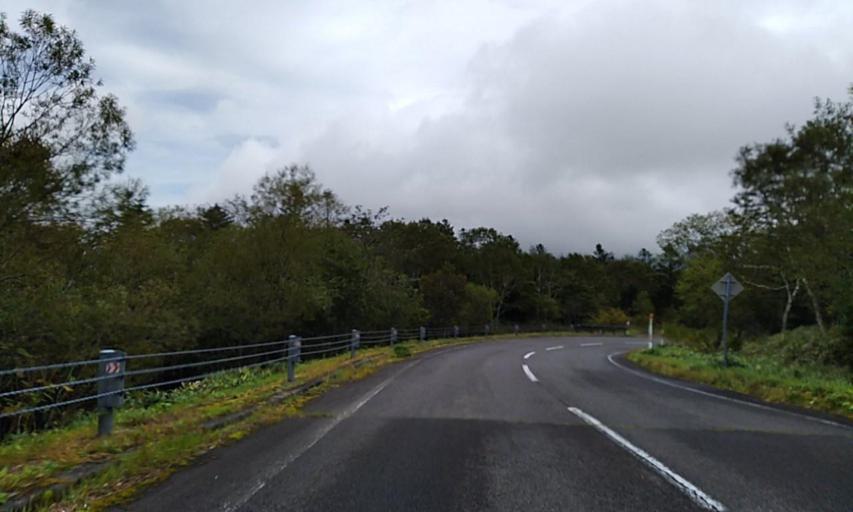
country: JP
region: Hokkaido
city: Abashiri
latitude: 43.6035
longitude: 144.5795
